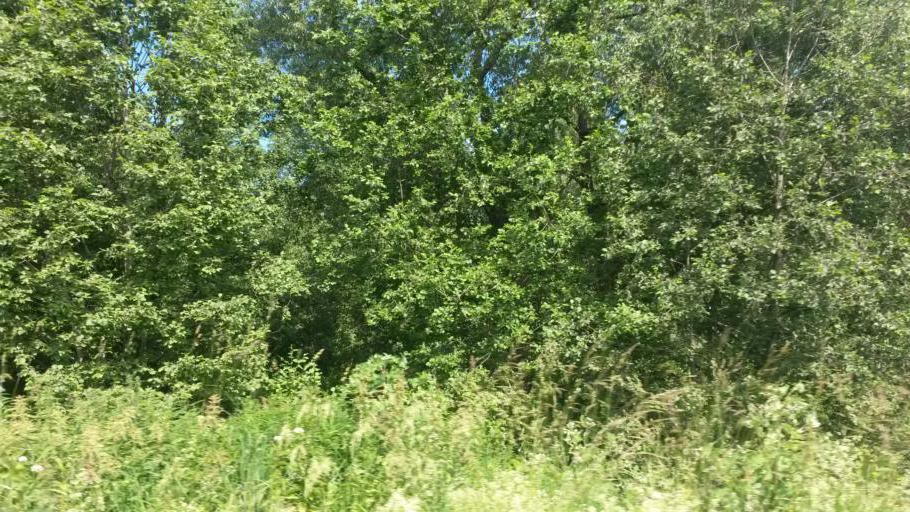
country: RU
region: Jaroslavl
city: Dubki
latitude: 57.3327
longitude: 40.2174
